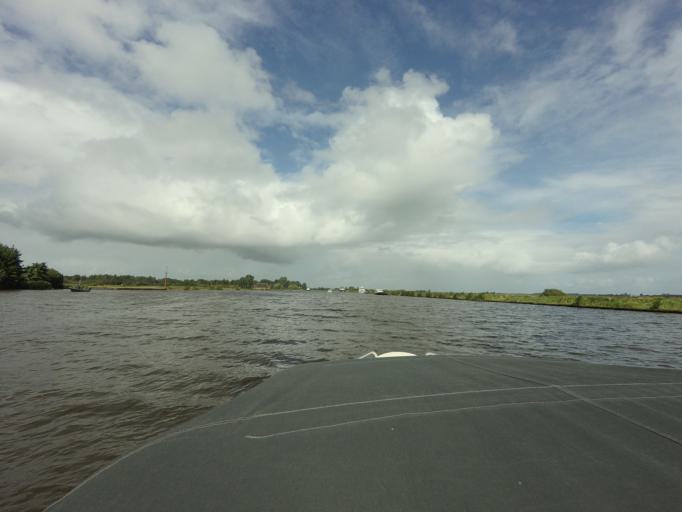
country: NL
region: Friesland
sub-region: Gemeente Boarnsterhim
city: Warten
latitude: 53.1348
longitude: 5.9189
